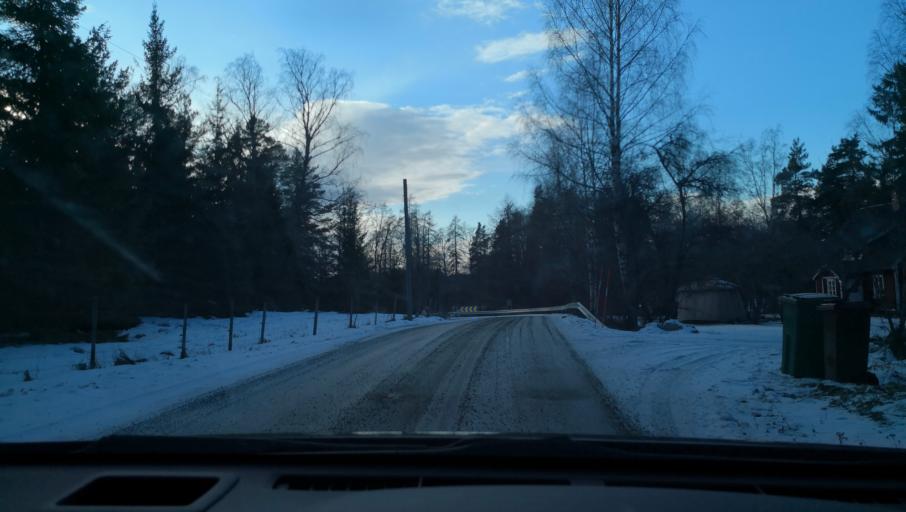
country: SE
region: Uppsala
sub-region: Enkopings Kommun
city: Irsta
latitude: 59.6591
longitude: 16.7869
